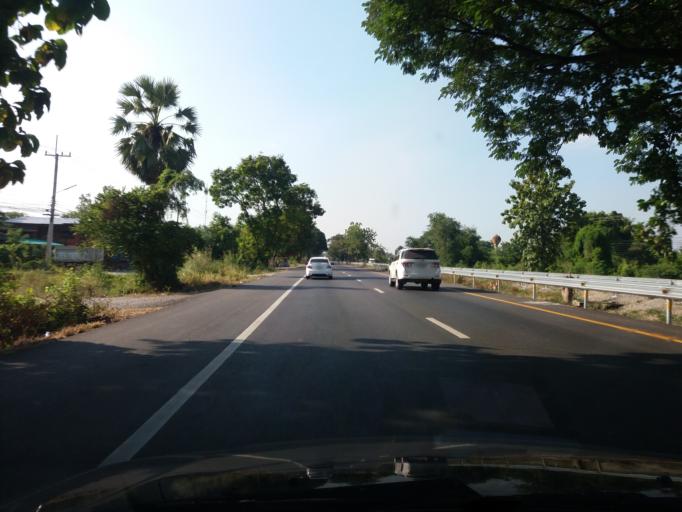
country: TH
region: Nakhon Sawan
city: Kao Liao
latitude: 15.7992
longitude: 99.9580
